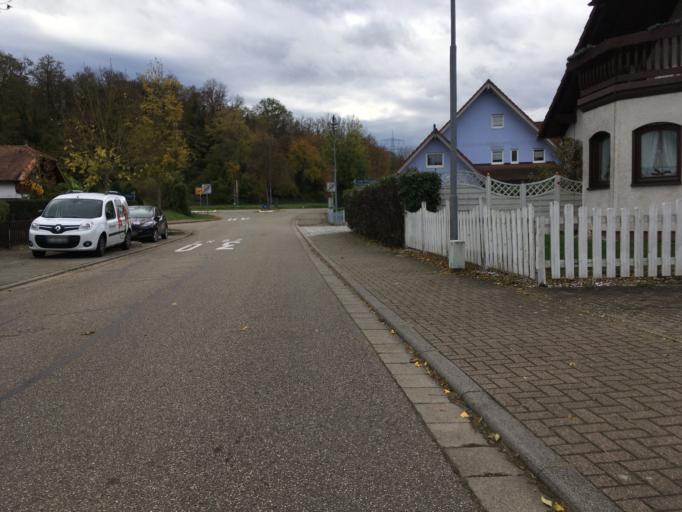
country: DE
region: Baden-Wuerttemberg
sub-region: Freiburg Region
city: Riegel
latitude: 48.1489
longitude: 7.7396
